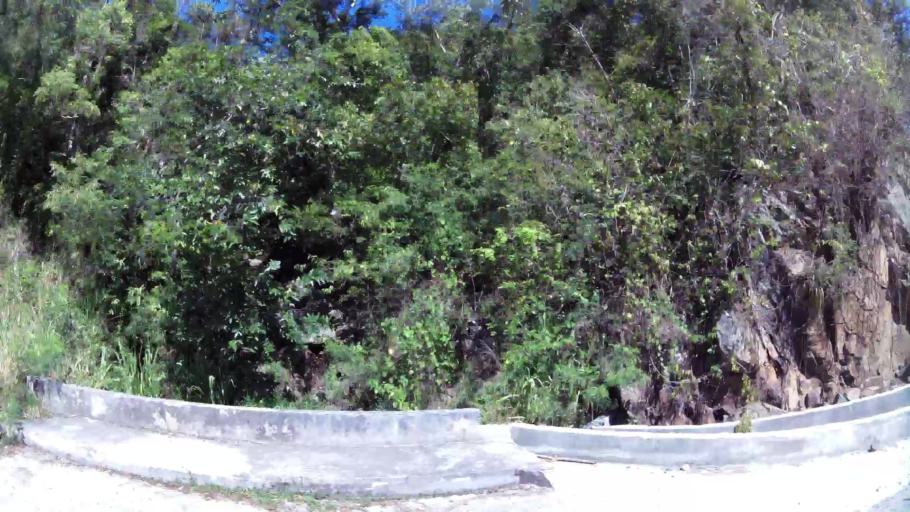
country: VG
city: Tortola
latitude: 18.4320
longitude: -64.6011
